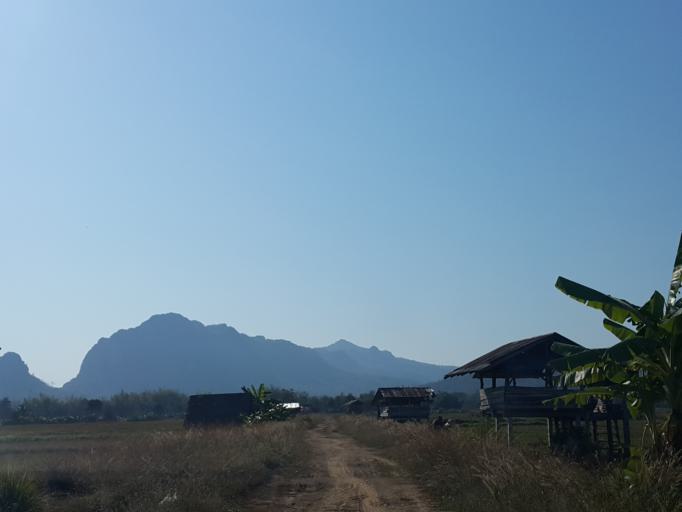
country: TH
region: Sukhothai
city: Thung Saliam
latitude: 17.3182
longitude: 99.4342
